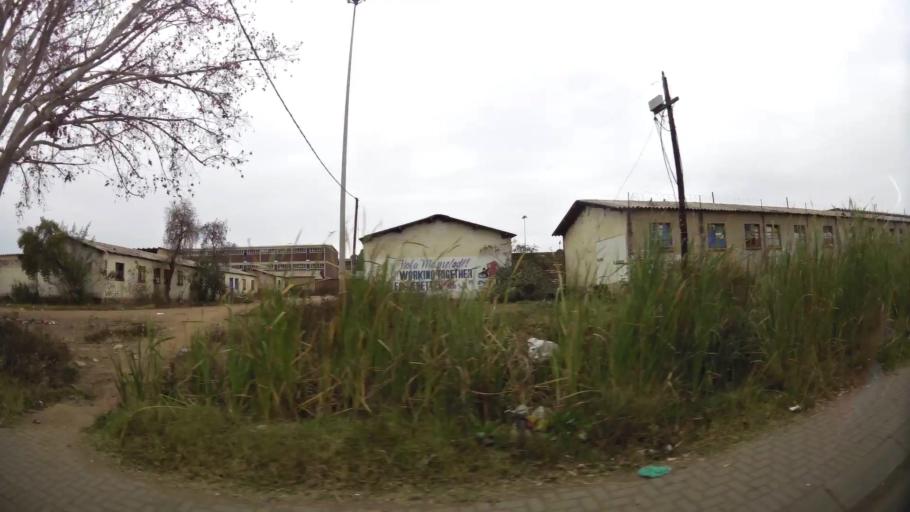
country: ZA
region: Gauteng
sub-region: City of Tshwane Metropolitan Municipality
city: Pretoria
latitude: -25.7145
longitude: 28.3395
